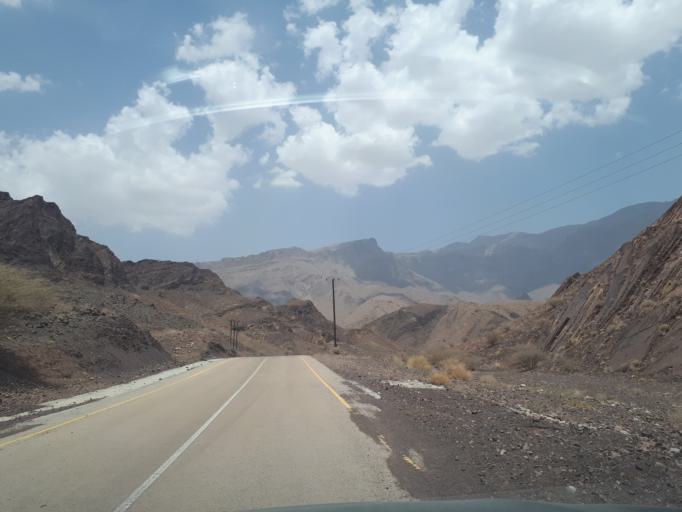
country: OM
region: Ash Sharqiyah
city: Badiyah
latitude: 22.4860
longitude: 59.1234
